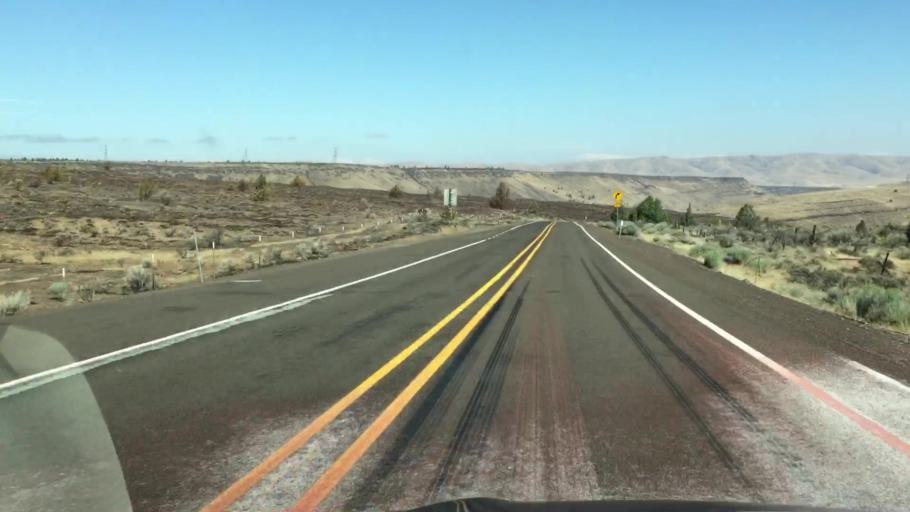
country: US
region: Oregon
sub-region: Jefferson County
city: Warm Springs
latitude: 45.1614
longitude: -121.0717
